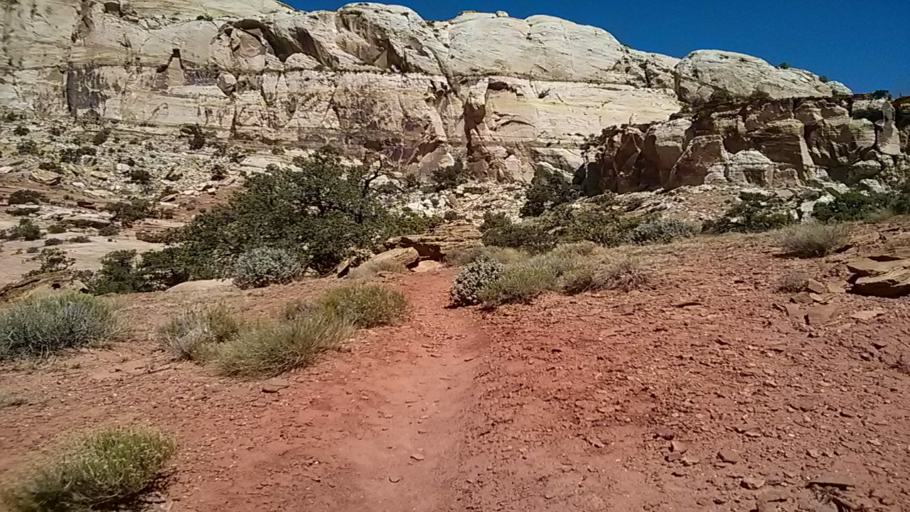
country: US
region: Utah
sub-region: Wayne County
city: Loa
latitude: 38.3052
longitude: -111.2620
